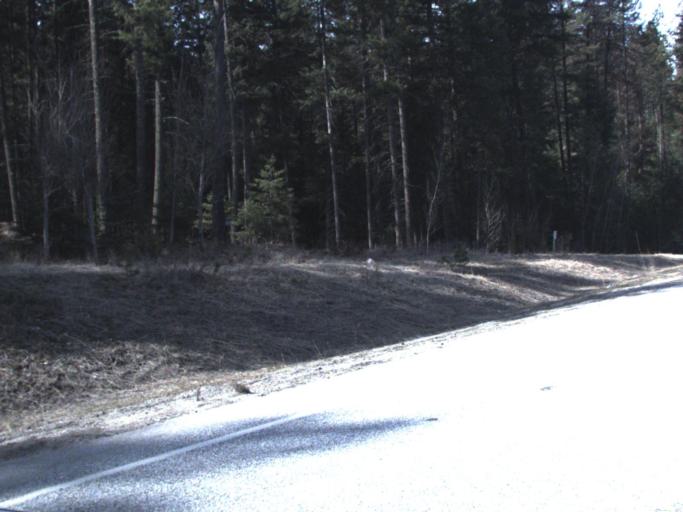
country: US
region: Washington
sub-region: Stevens County
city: Colville
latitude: 48.5412
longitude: -117.8427
